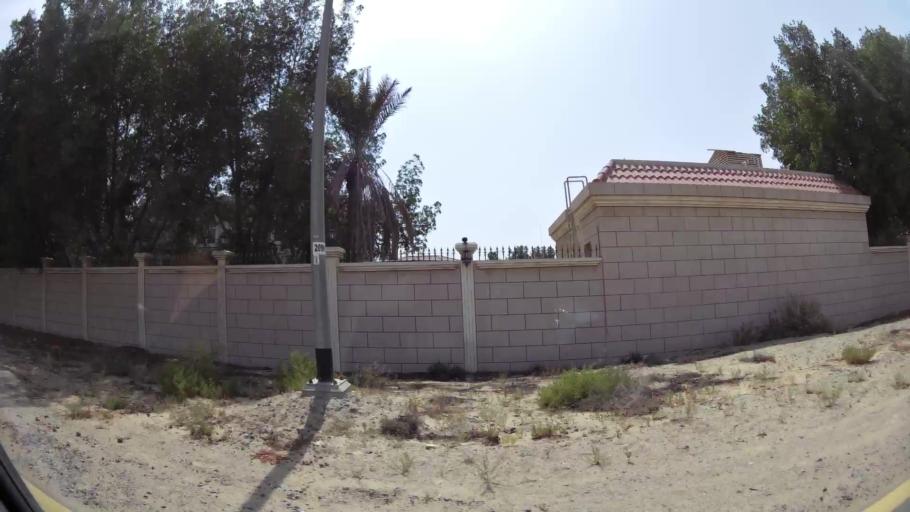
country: AE
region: Ash Shariqah
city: Sharjah
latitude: 25.2511
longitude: 55.4808
